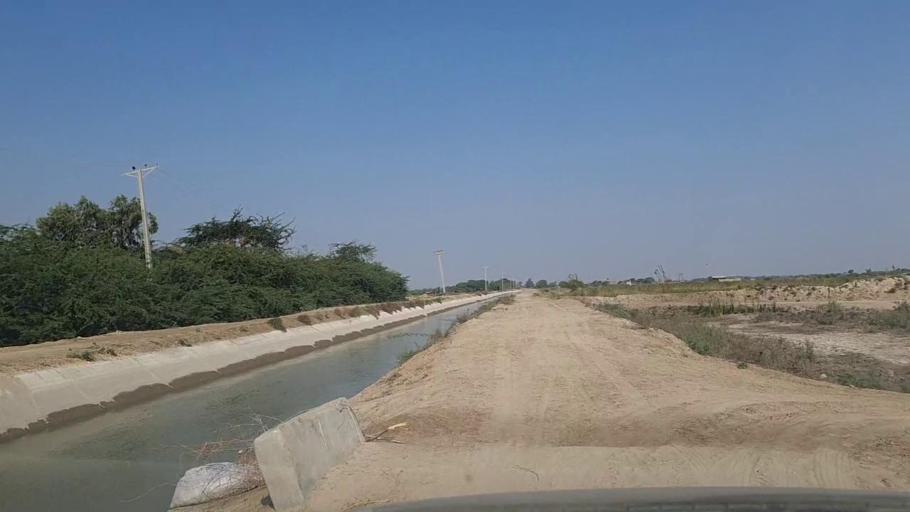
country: PK
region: Sindh
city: Mirpur Sakro
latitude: 24.5249
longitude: 67.8108
